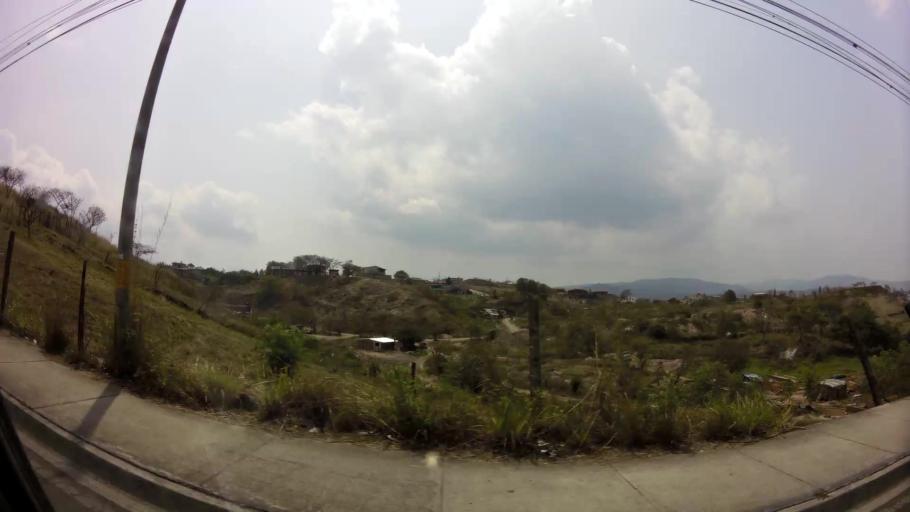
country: HN
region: Francisco Morazan
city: Yaguacire
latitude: 14.0464
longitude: -87.2244
